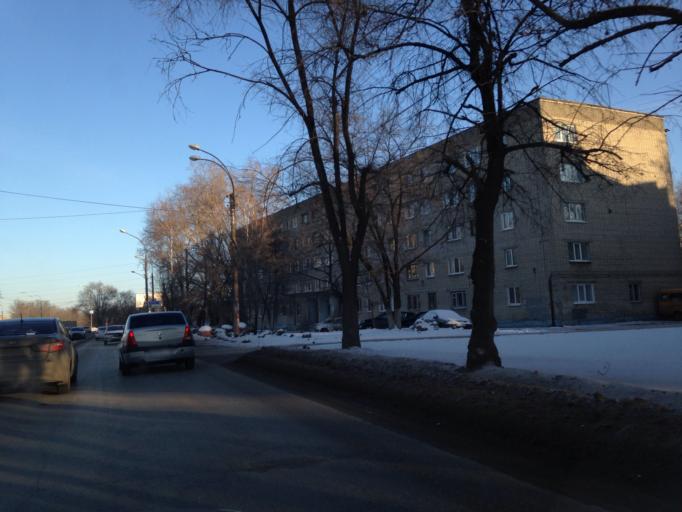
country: RU
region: Ulyanovsk
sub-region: Ulyanovskiy Rayon
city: Ulyanovsk
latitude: 54.2895
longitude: 48.3675
